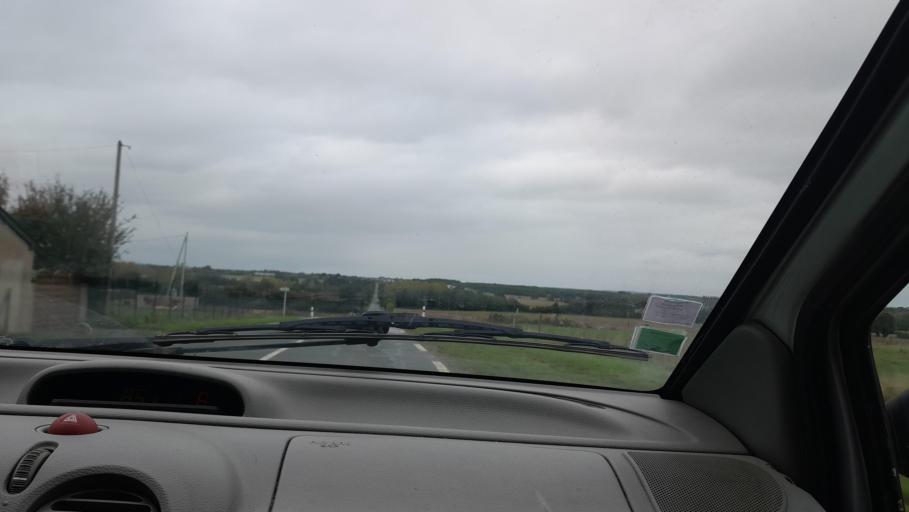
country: FR
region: Pays de la Loire
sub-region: Departement de la Loire-Atlantique
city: Saint-Mars-la-Jaille
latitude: 47.5547
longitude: -1.1857
